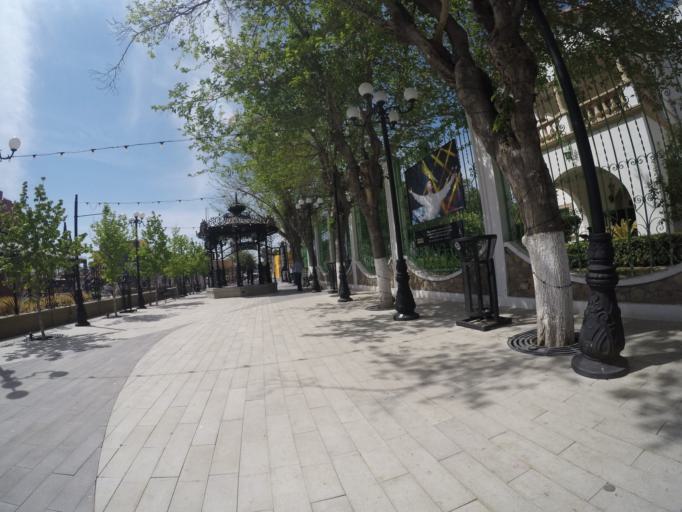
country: MX
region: Chihuahua
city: Ciudad Juarez
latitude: 31.7387
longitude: -106.4693
